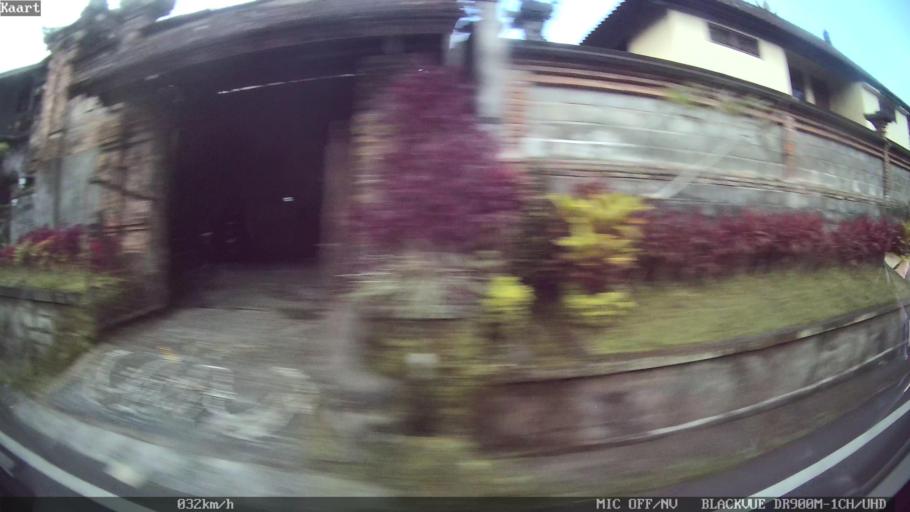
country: ID
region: Bali
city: Banjar Pesalakan
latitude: -8.4925
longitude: 115.2979
